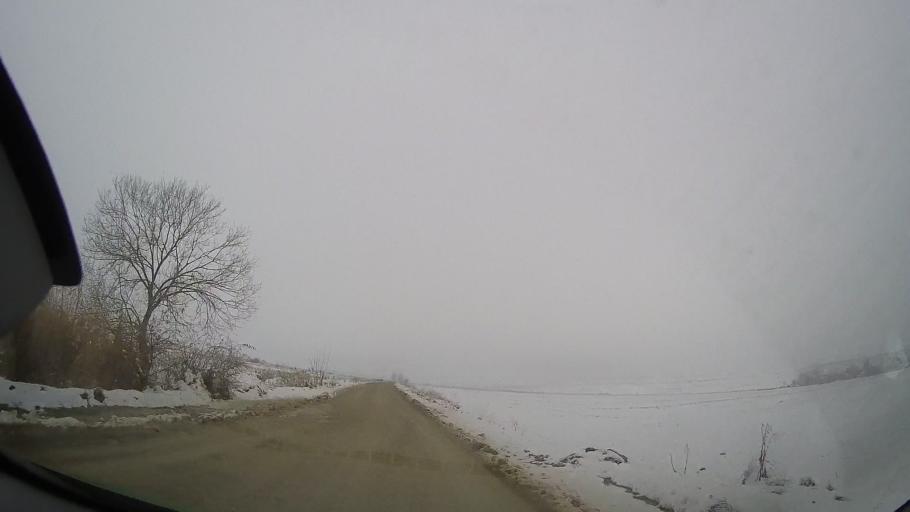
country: RO
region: Vaslui
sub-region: Comuna Todiresti
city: Todiresti
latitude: 46.8810
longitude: 27.3715
